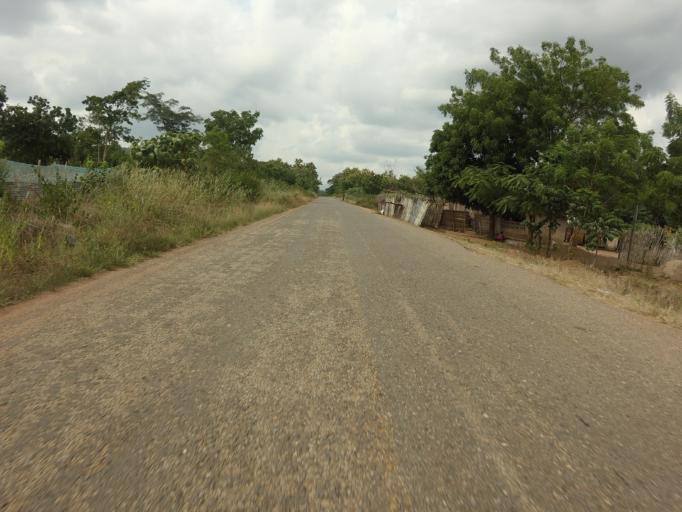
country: GH
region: Volta
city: Ho
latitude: 6.6662
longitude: 0.3514
